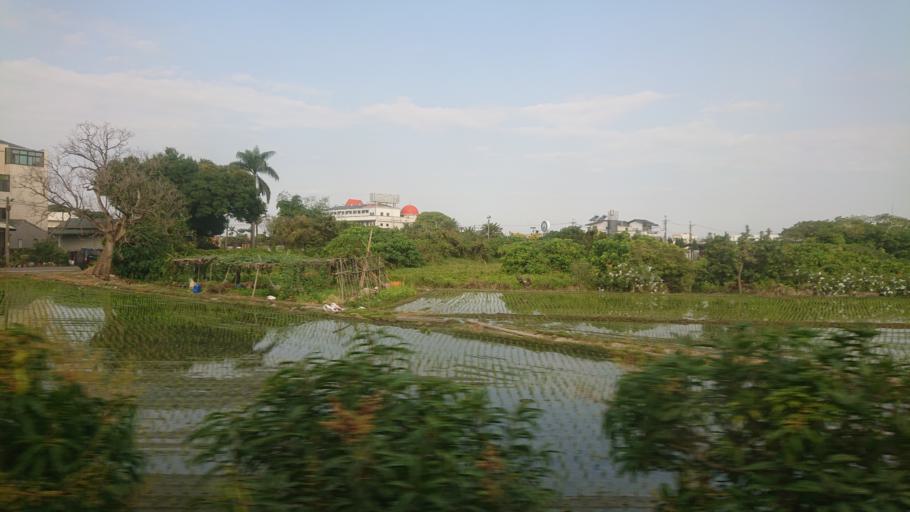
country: TW
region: Taiwan
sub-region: Yunlin
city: Douliu
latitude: 23.7016
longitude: 120.5284
